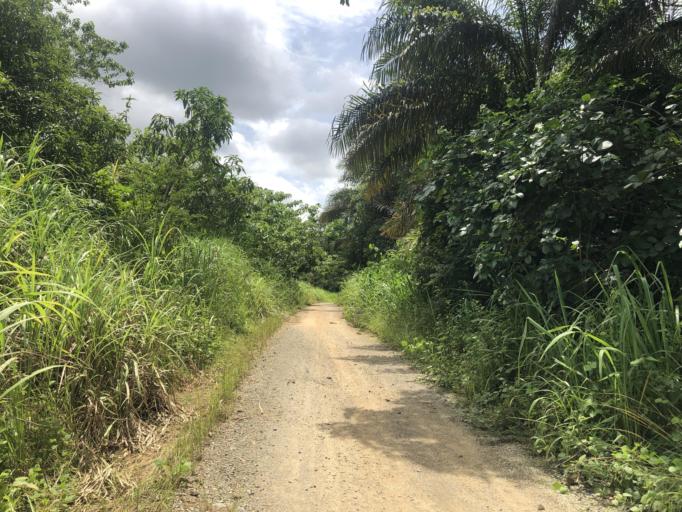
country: SL
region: Northern Province
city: Bumbuna
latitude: 9.0008
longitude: -11.7652
